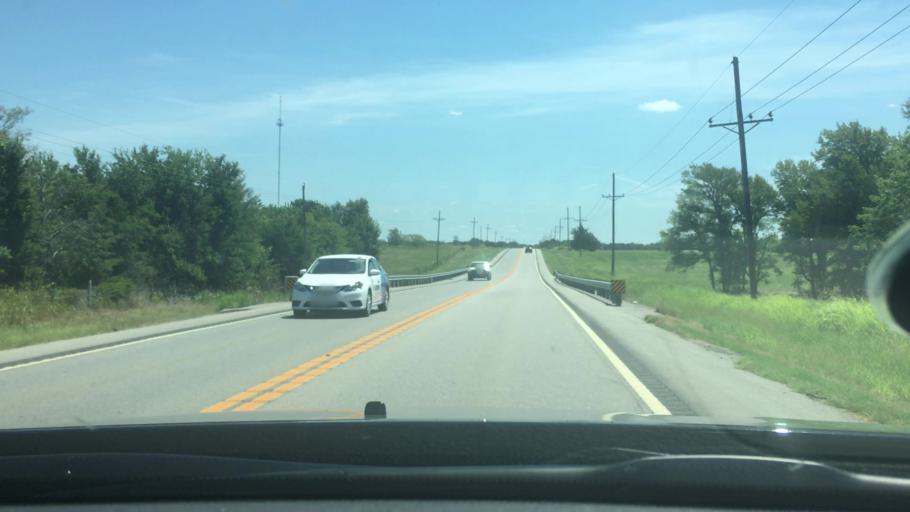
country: US
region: Oklahoma
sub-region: Bryan County
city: Durant
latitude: 33.9975
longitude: -96.2768
